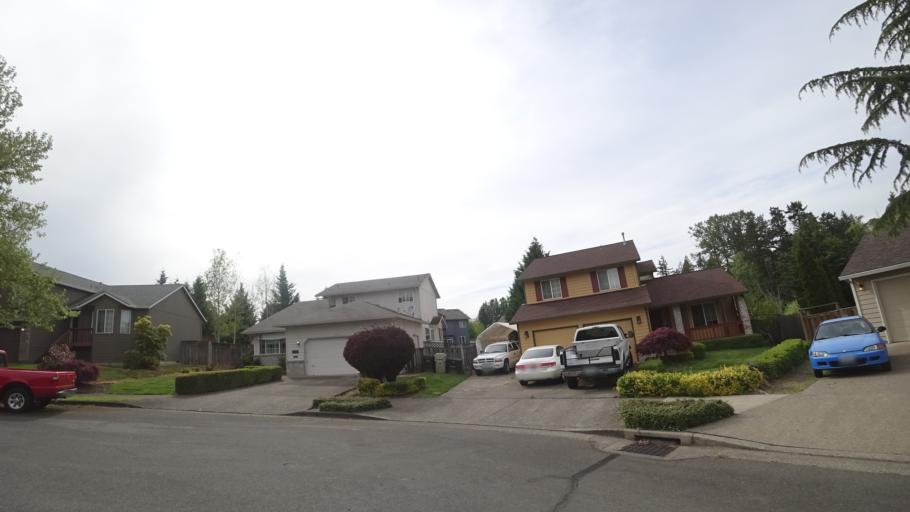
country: US
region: Oregon
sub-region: Washington County
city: Aloha
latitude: 45.5085
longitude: -122.9253
